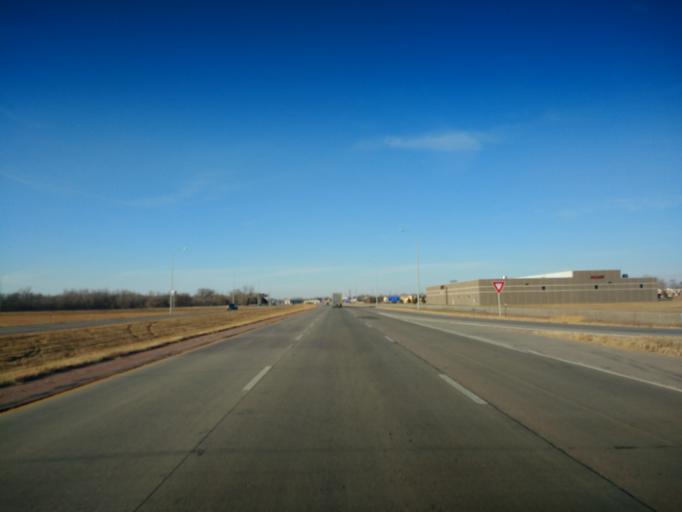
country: US
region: South Dakota
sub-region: Union County
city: Dakota Dunes
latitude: 42.5059
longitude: -96.4907
